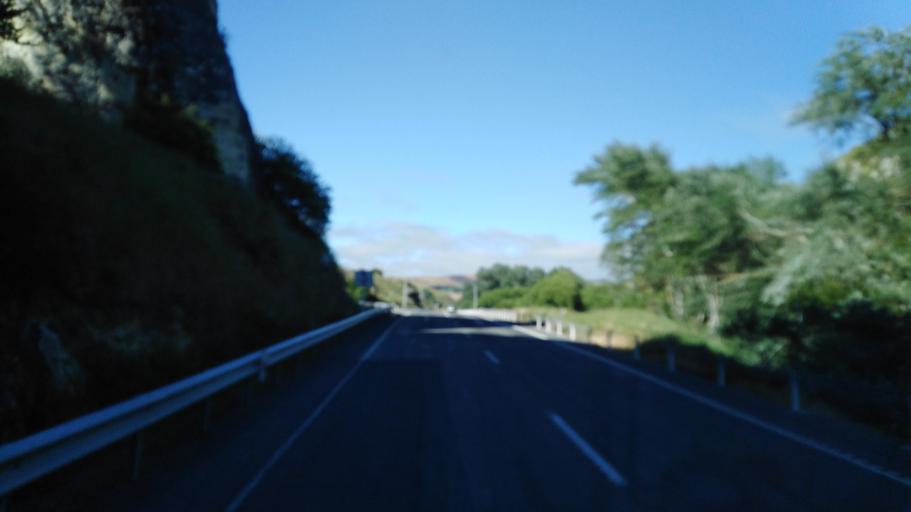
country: NZ
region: Canterbury
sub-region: Hurunui District
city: Amberley
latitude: -42.9997
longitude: 172.7141
